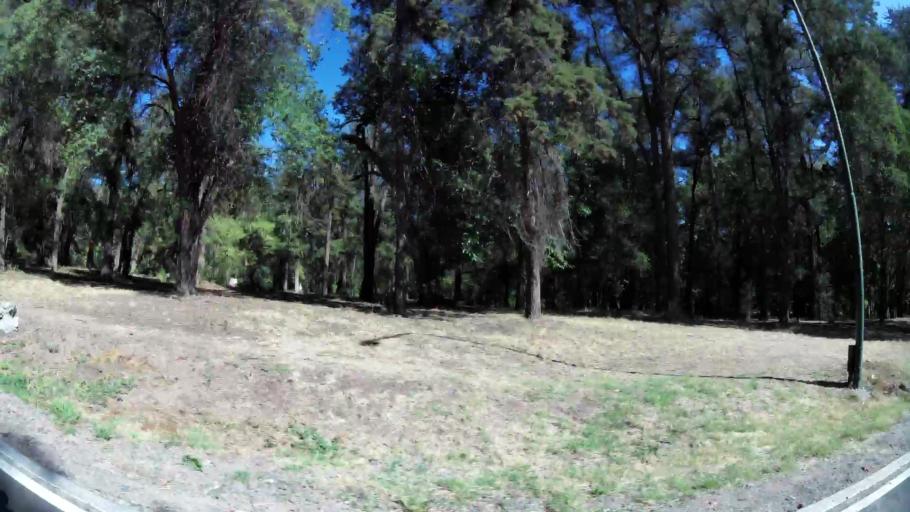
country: AR
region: Mendoza
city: Mendoza
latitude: -32.8902
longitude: -68.8731
